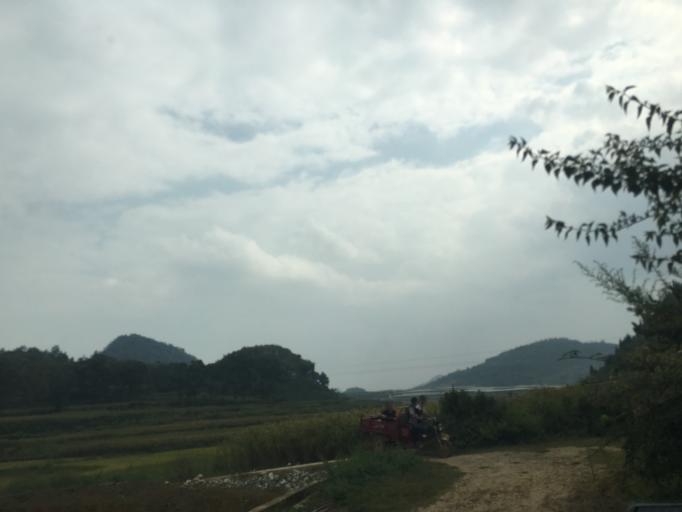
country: CN
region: Guangxi Zhuangzu Zizhiqu
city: Xinzhou
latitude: 25.4913
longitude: 105.6521
